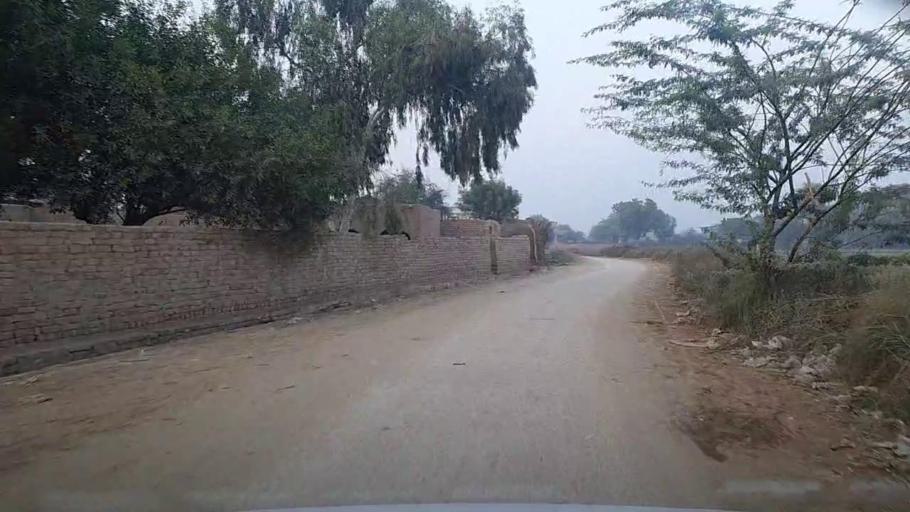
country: PK
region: Sindh
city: Bozdar
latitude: 27.0714
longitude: 68.5981
